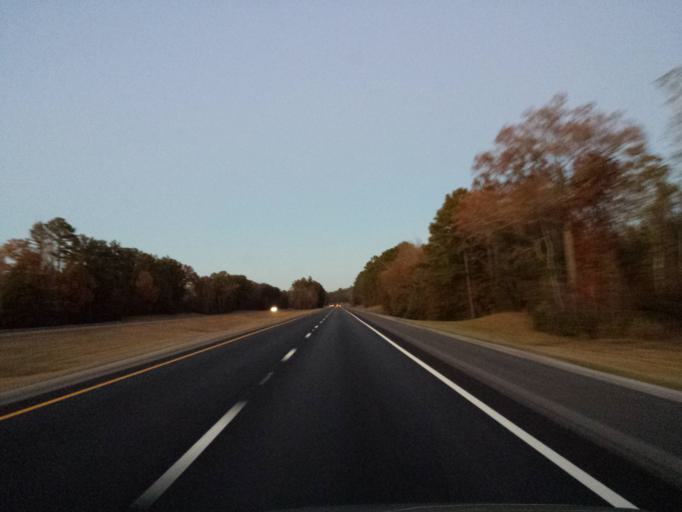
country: US
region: Mississippi
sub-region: Jones County
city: Sharon
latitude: 31.7542
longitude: -89.0704
